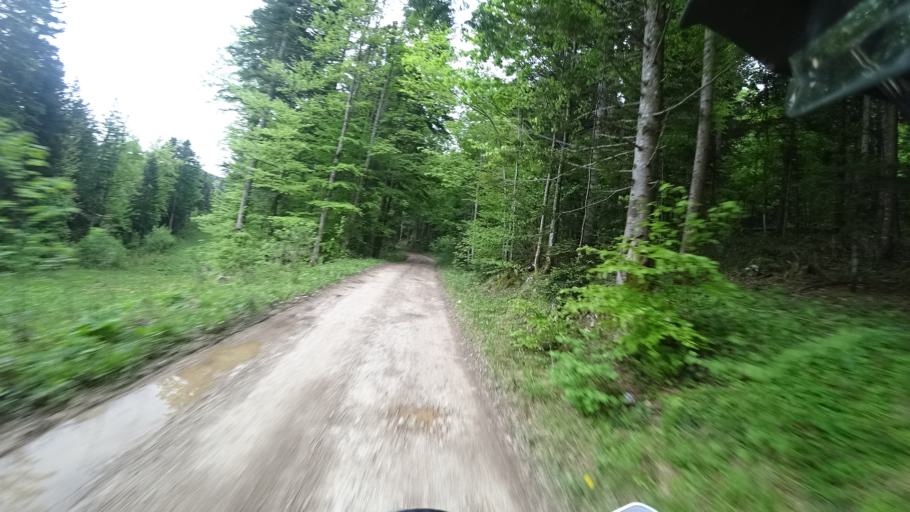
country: HR
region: Karlovacka
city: Plaski
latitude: 44.9616
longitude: 15.4076
